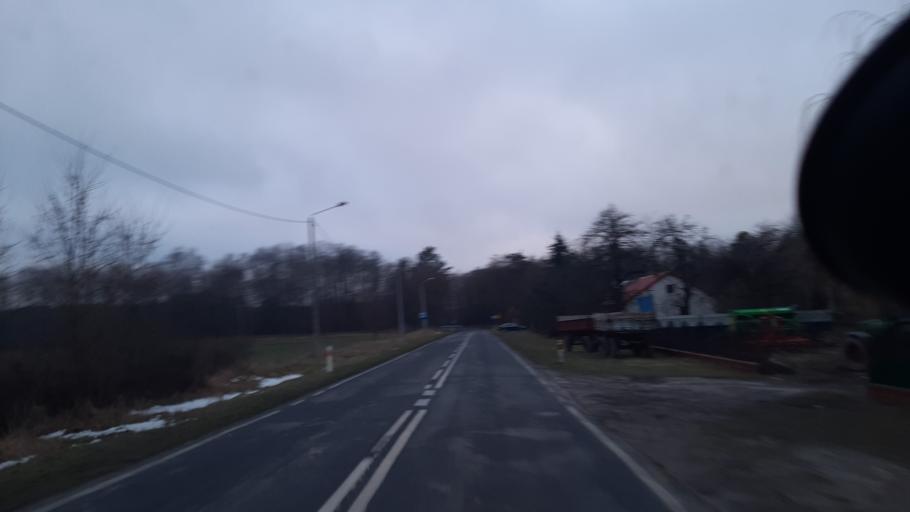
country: PL
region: Lublin Voivodeship
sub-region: Powiat parczewski
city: Debowa Kloda
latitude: 51.6393
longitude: 23.0275
